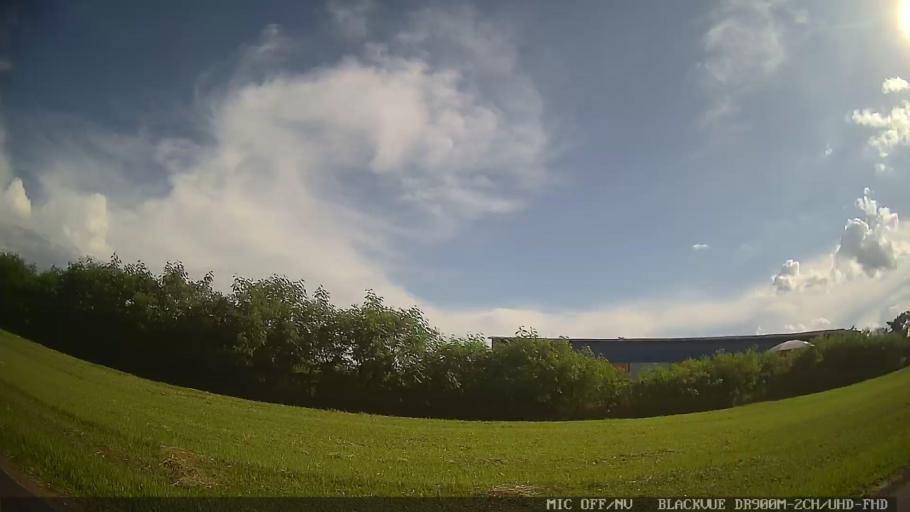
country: BR
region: Sao Paulo
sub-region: Laranjal Paulista
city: Laranjal Paulista
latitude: -23.0779
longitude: -47.8040
